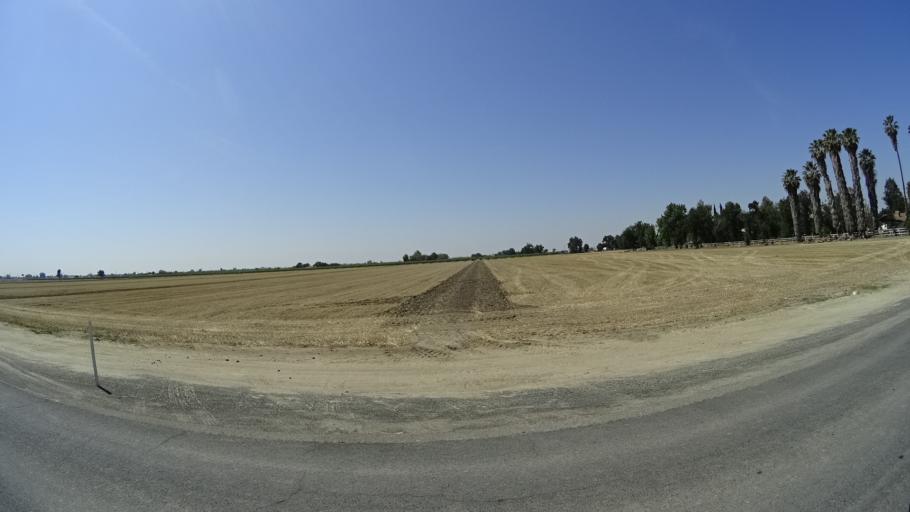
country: US
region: California
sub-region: Kings County
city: Lemoore
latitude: 36.3280
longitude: -119.8159
